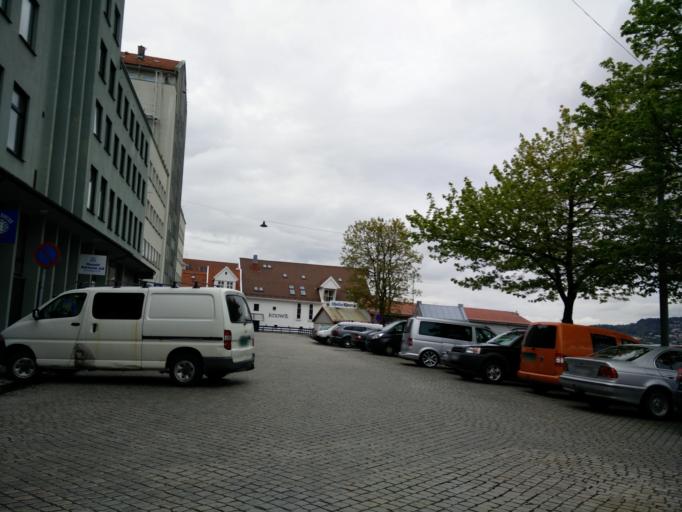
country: NO
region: Hordaland
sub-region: Bergen
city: Bergen
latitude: 60.3991
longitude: 5.3097
